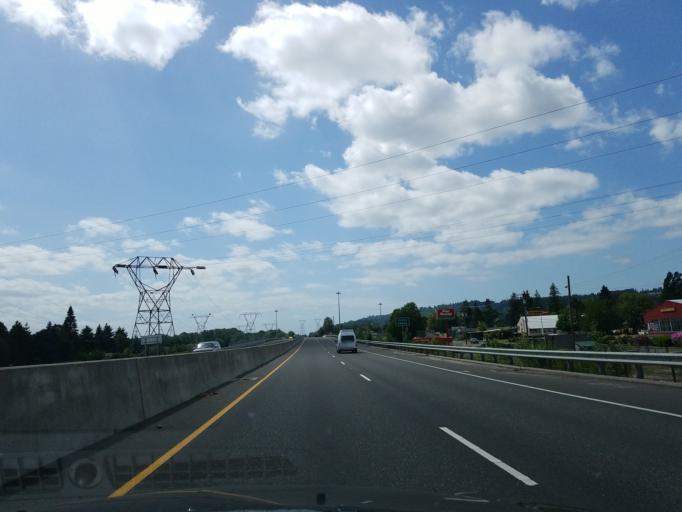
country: US
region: Washington
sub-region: Clark County
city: Camas
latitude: 45.5805
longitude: -122.3812
